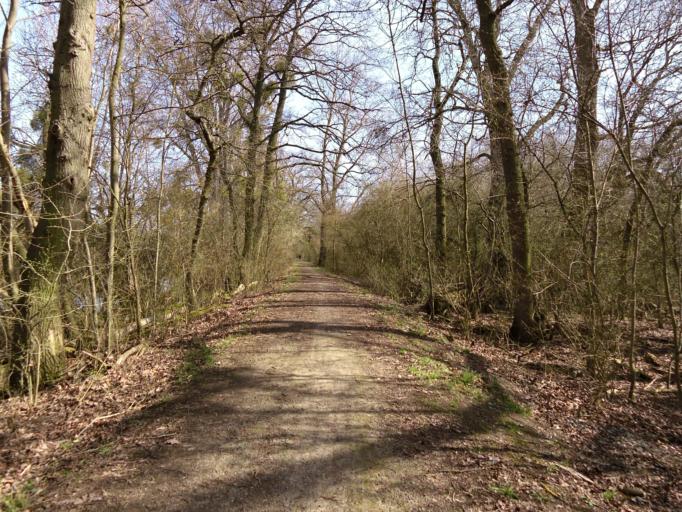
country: DE
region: Rheinland-Pfalz
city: Gimbsheim
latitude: 49.8118
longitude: 8.4009
